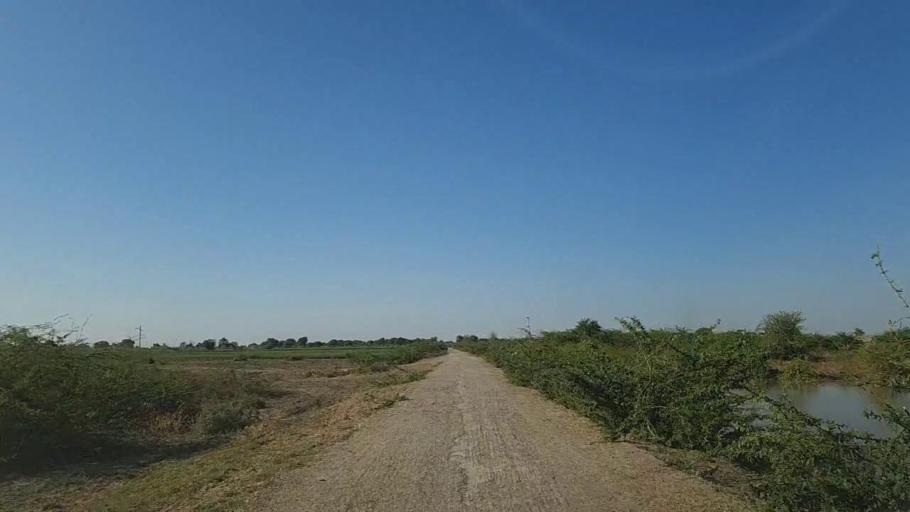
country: PK
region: Sindh
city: Samaro
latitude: 25.2572
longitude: 69.4901
